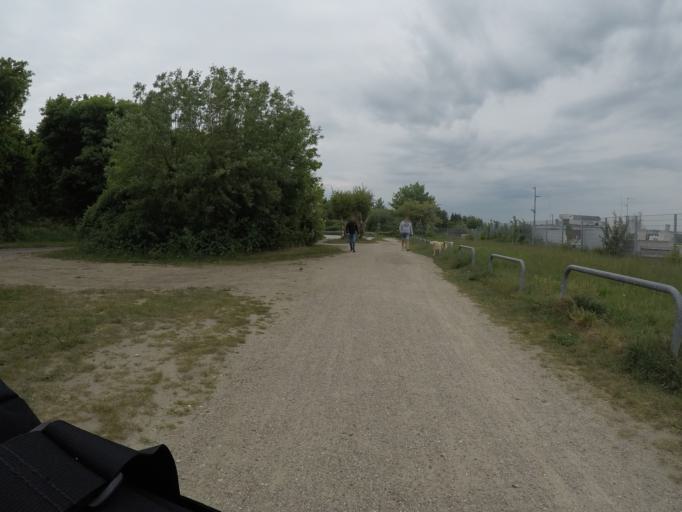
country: DE
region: Hamburg
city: Langenhorn
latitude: 53.6459
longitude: 9.9789
